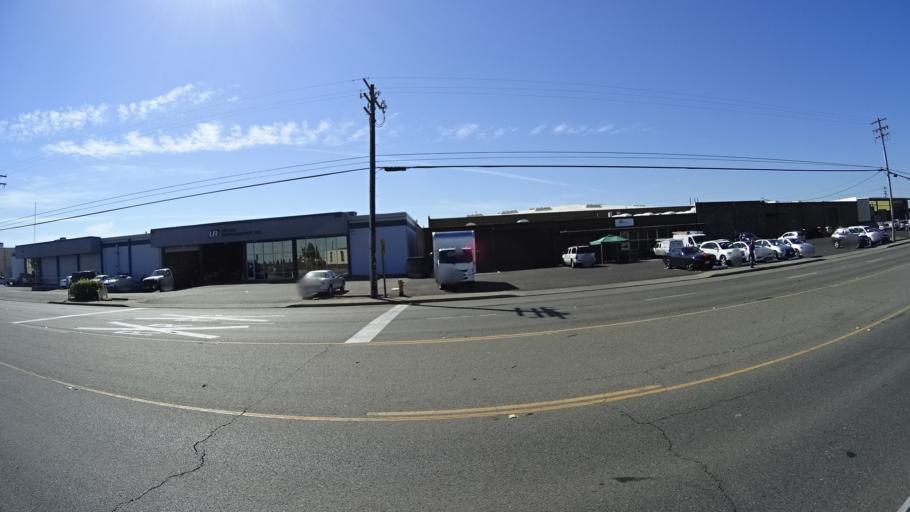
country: US
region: California
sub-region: Sacramento County
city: North Highlands
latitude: 38.6464
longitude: -121.3966
